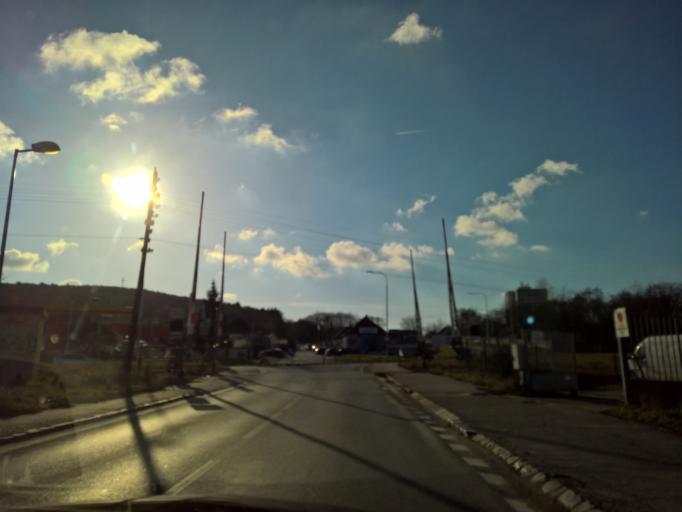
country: SK
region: Nitriansky
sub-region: Okres Nitra
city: Nitra
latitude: 48.3072
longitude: 18.0718
